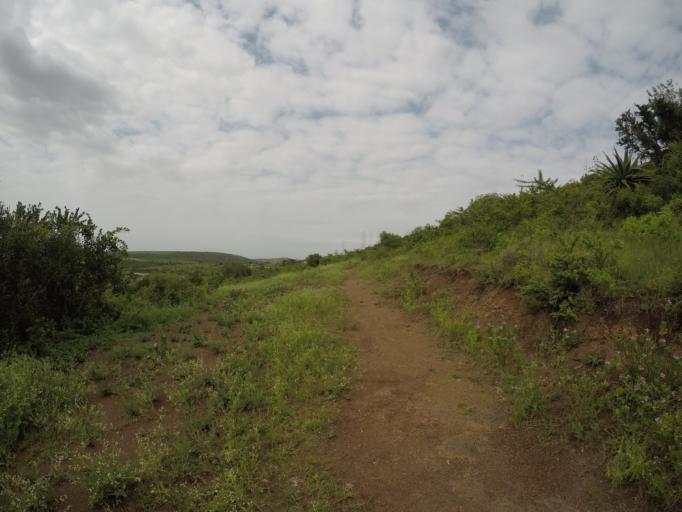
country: ZA
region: KwaZulu-Natal
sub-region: uThungulu District Municipality
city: Empangeni
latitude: -28.6323
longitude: 31.9097
